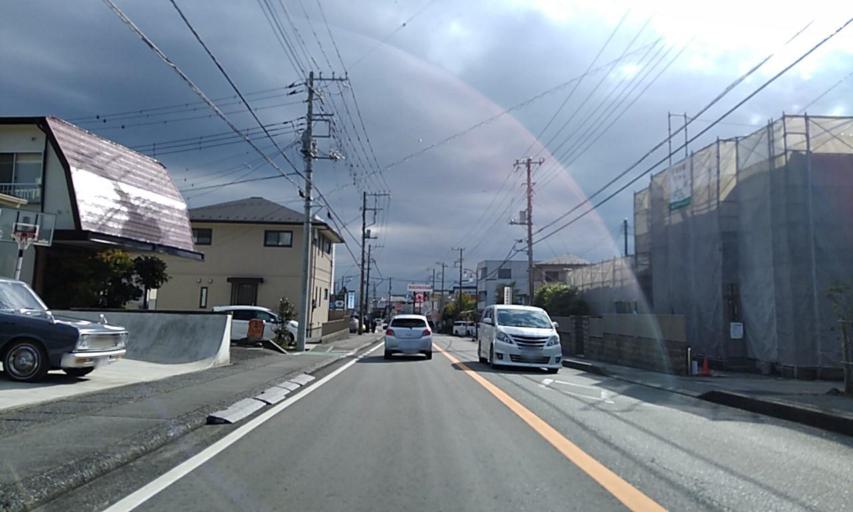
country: JP
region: Shizuoka
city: Gotemba
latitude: 35.2938
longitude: 138.9285
